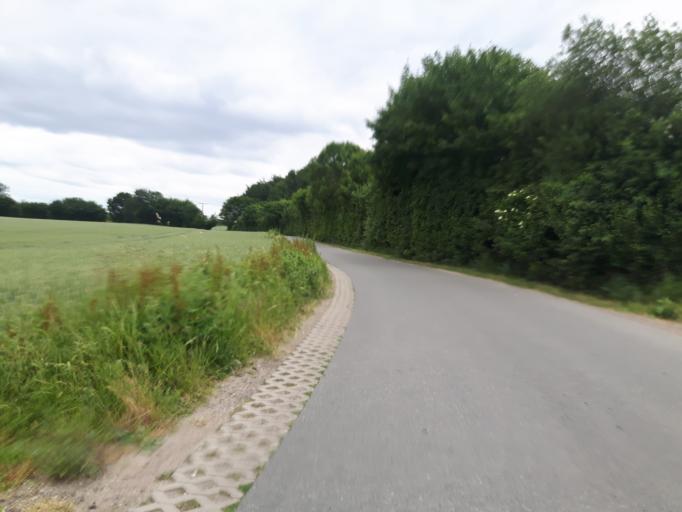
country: DE
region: Schleswig-Holstein
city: Schashagen
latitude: 54.1246
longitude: 10.9067
